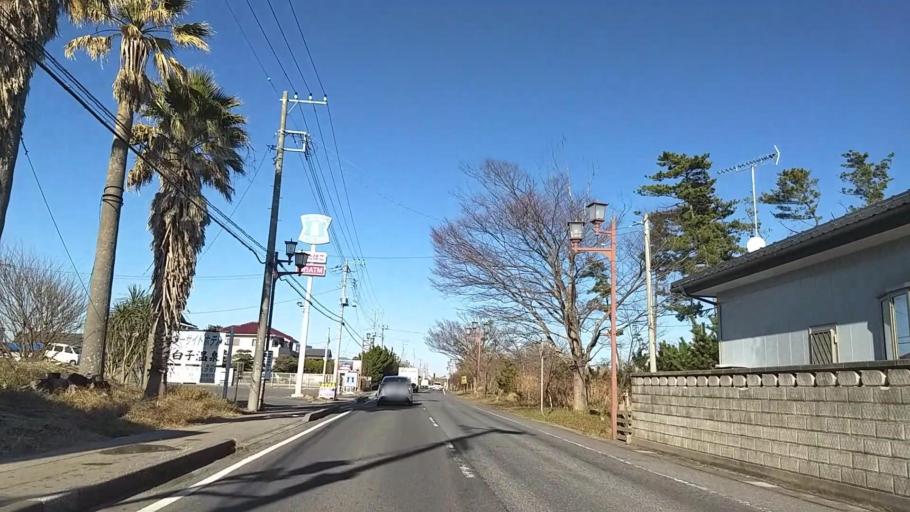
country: JP
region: Chiba
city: Mobara
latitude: 35.4317
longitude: 140.3964
